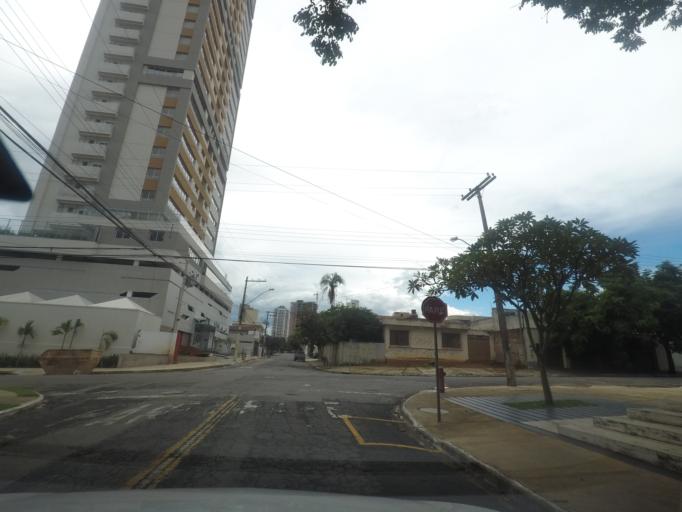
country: BR
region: Goias
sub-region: Goiania
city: Goiania
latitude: -16.6944
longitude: -49.2676
